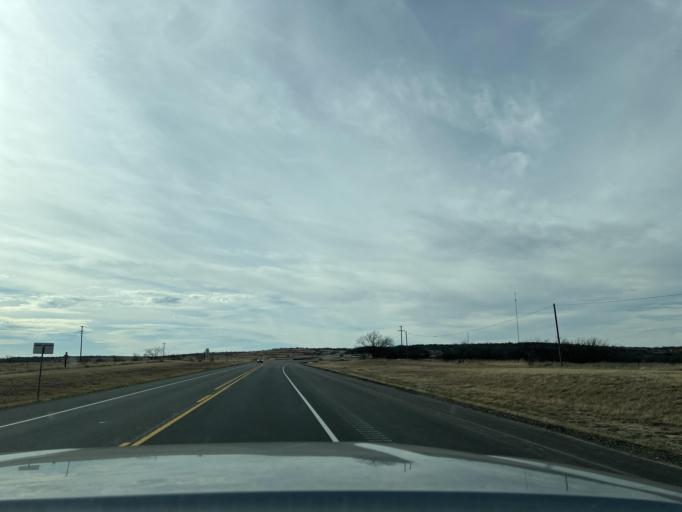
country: US
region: Texas
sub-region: Shackelford County
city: Albany
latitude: 32.7051
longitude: -99.4057
